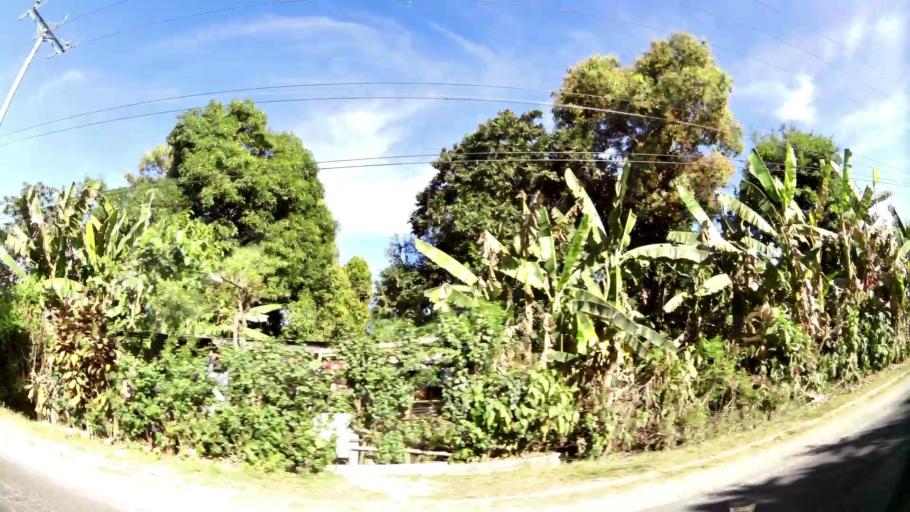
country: SV
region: Cuscatlan
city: Tecoluca
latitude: 13.8104
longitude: -89.0357
